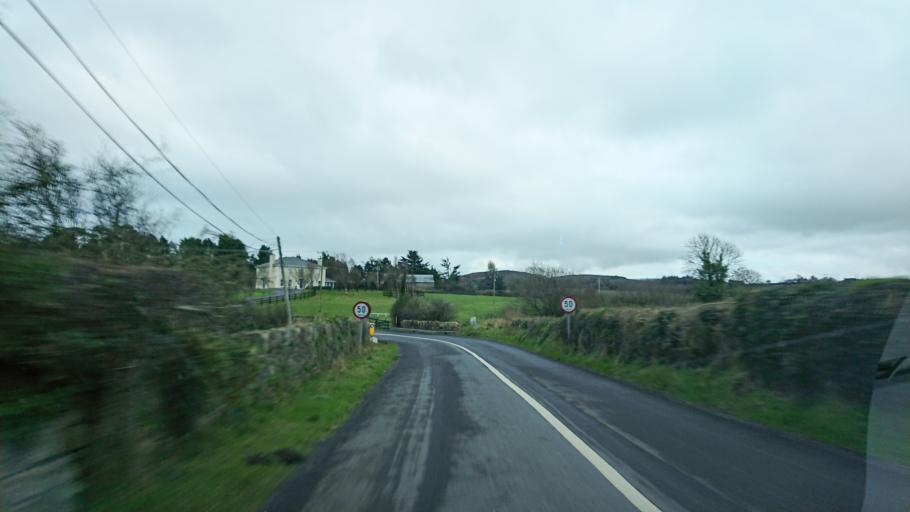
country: IE
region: Munster
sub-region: Waterford
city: Portlaw
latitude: 52.1732
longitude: -7.4028
